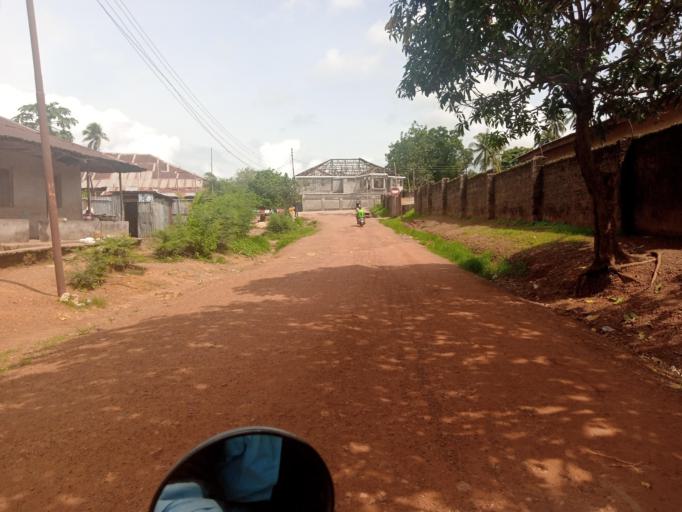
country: SL
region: Southern Province
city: Bo
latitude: 7.9695
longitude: -11.7396
